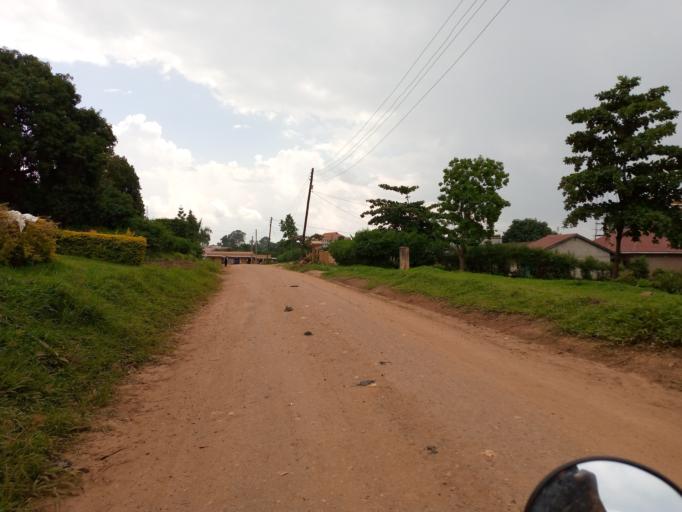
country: UG
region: Eastern Region
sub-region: Mbale District
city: Mbale
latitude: 1.0821
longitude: 34.1730
